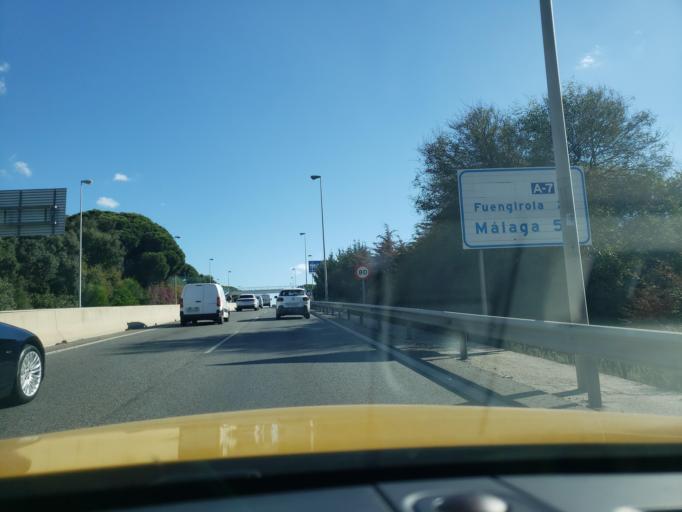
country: ES
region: Andalusia
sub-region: Provincia de Malaga
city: Ojen
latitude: 36.5038
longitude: -4.8093
